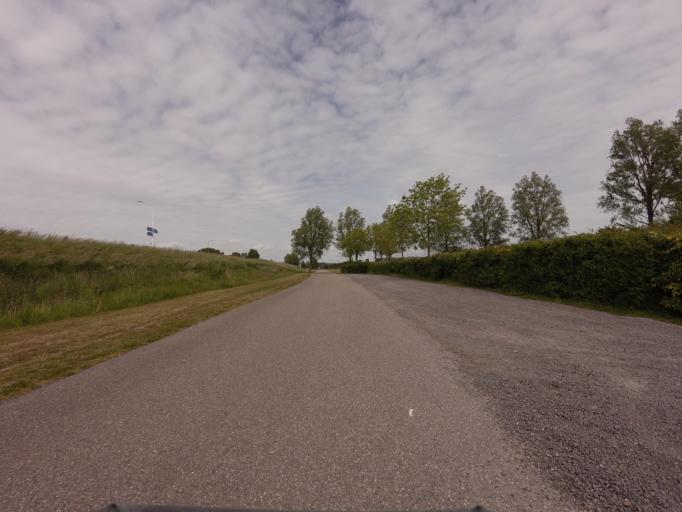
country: NL
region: North Holland
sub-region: Gemeente Medemblik
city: Medemblik
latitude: 52.7661
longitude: 5.1173
